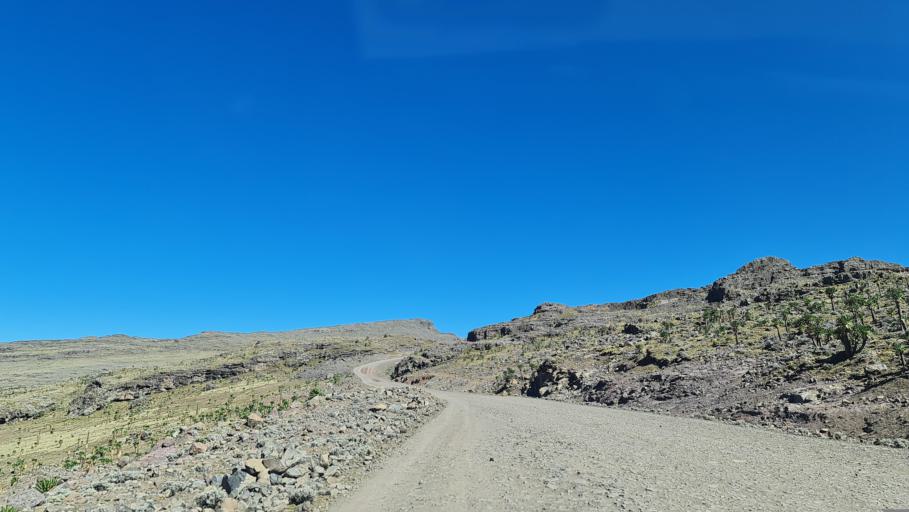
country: ET
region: Amhara
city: Debark'
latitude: 13.2194
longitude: 38.2202
